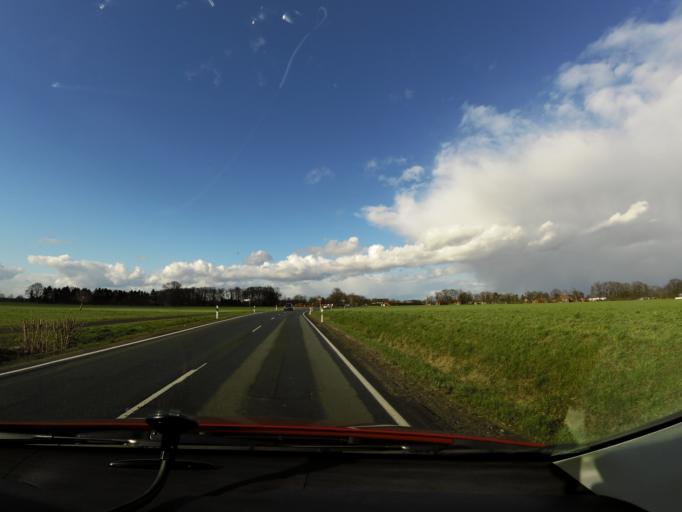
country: DE
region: North Rhine-Westphalia
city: Rietberg
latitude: 51.8622
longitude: 8.4480
